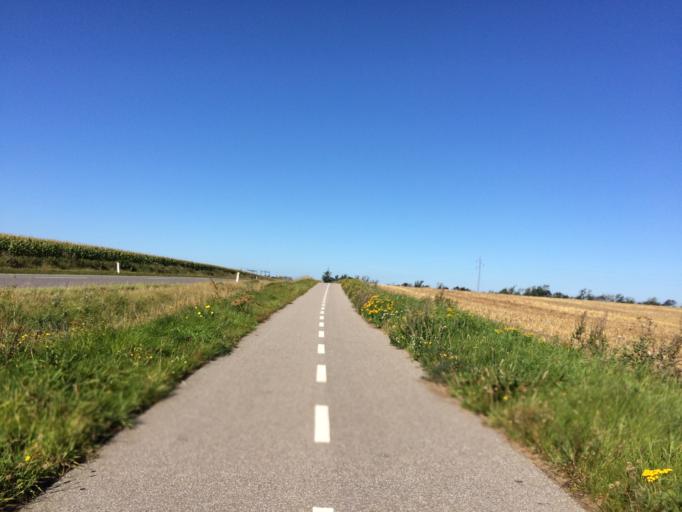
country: DK
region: Central Jutland
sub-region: Holstebro Kommune
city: Ulfborg
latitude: 56.2738
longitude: 8.2035
